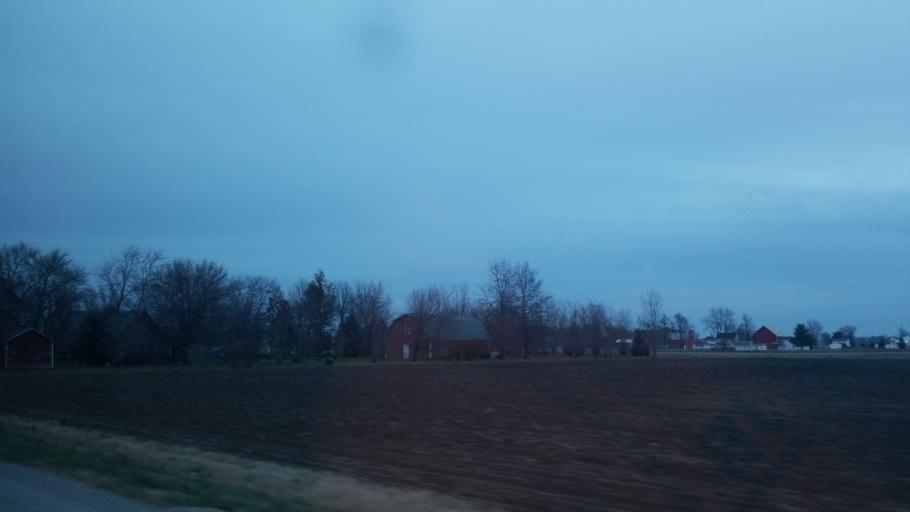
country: US
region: Indiana
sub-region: Adams County
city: Decatur
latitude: 40.7575
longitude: -84.9952
